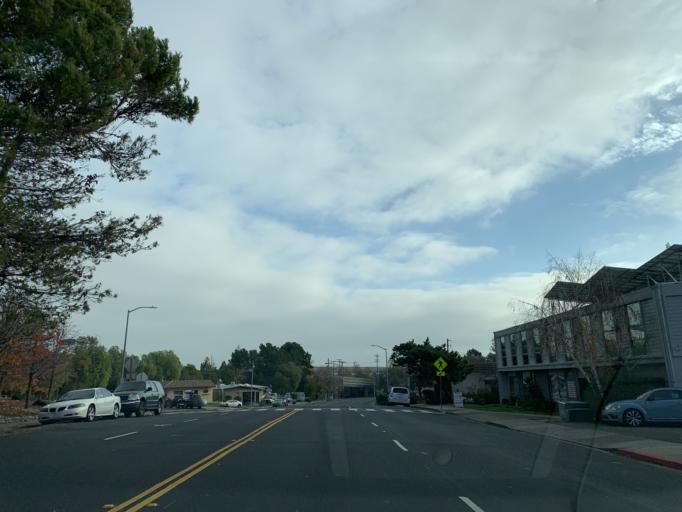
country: US
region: California
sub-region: Contra Costa County
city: Saranap
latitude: 37.8943
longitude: -122.0750
